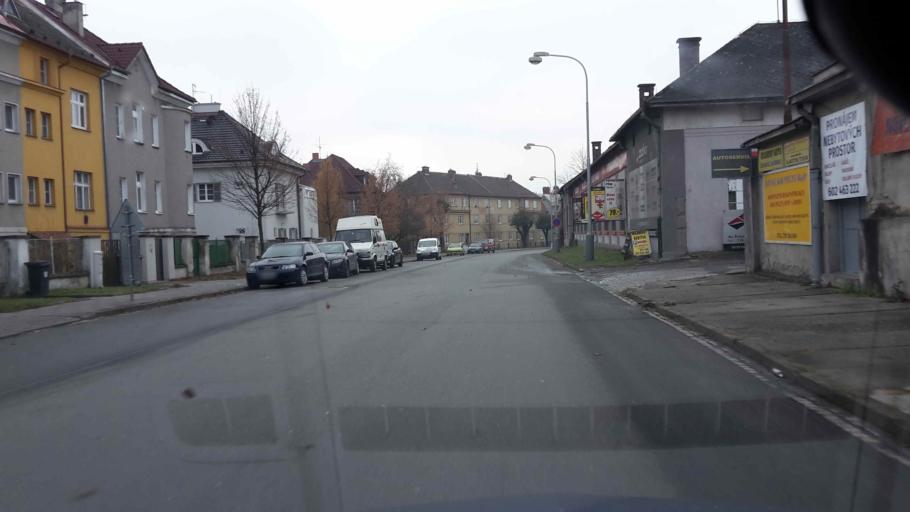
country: CZ
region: Olomoucky
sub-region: Okres Olomouc
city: Olomouc
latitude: 49.6001
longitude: 17.2371
